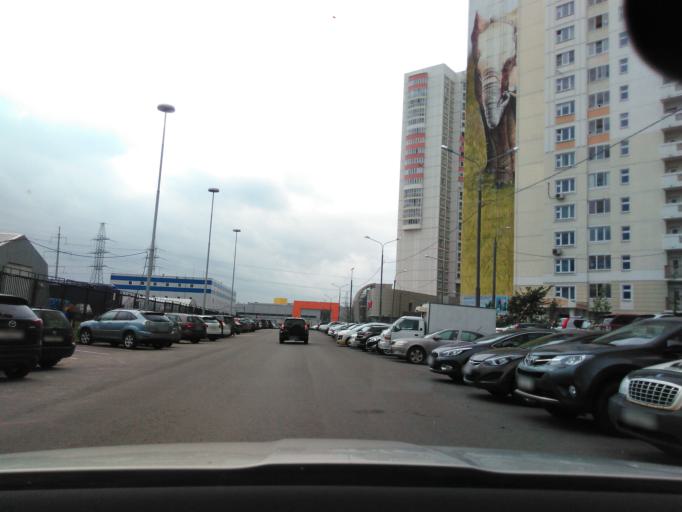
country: RU
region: Moscow
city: Khimki
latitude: 55.8853
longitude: 37.4348
